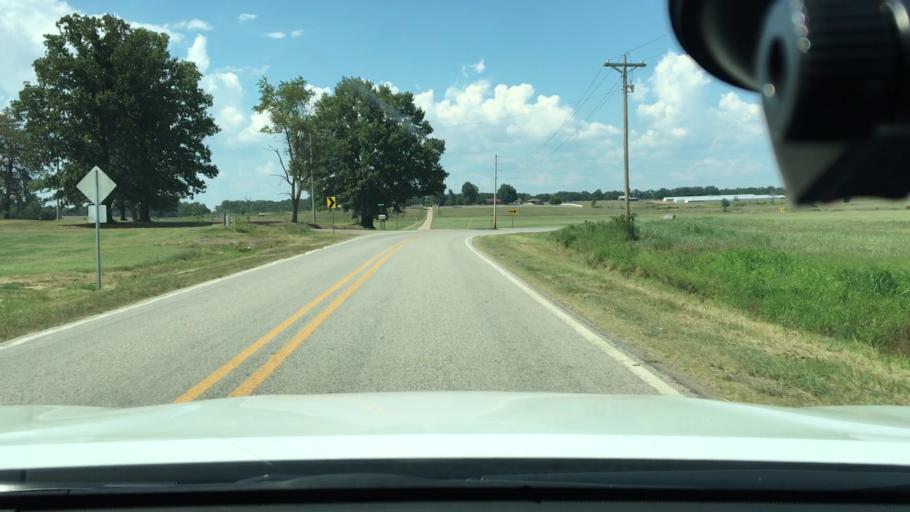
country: US
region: Arkansas
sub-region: Johnson County
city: Coal Hill
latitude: 35.3498
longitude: -93.5886
